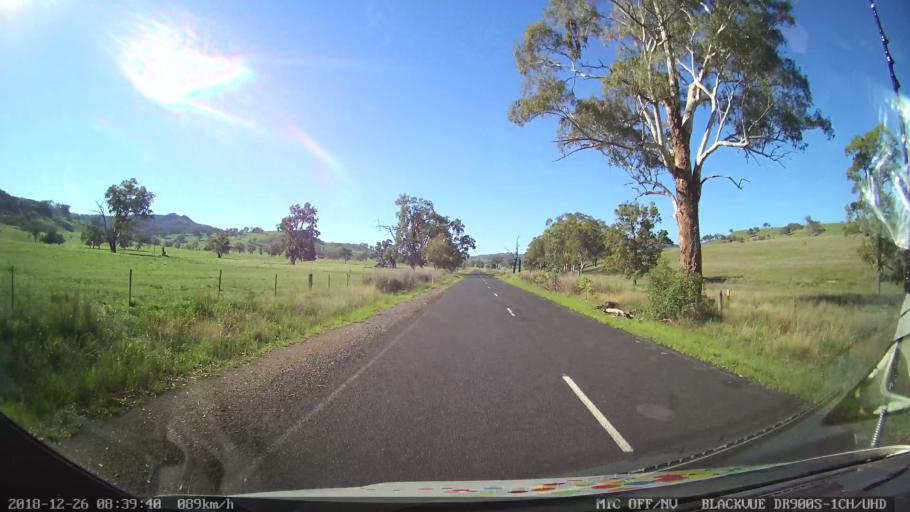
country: AU
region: New South Wales
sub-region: Mid-Western Regional
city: Kandos
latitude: -32.4565
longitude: 150.0756
